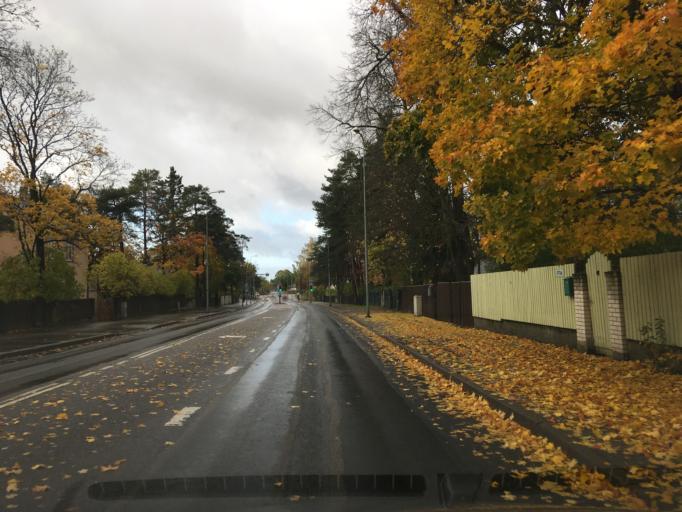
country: EE
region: Harju
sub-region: Saue vald
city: Laagri
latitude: 59.3712
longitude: 24.6407
